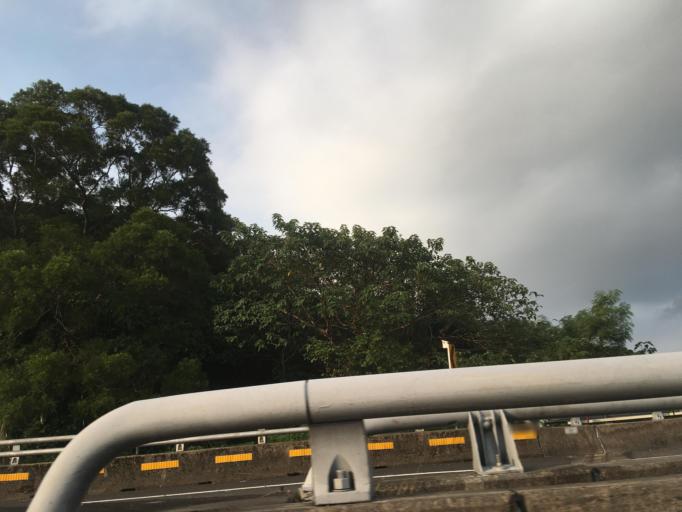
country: TW
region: Taipei
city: Taipei
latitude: 25.0362
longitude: 121.6196
